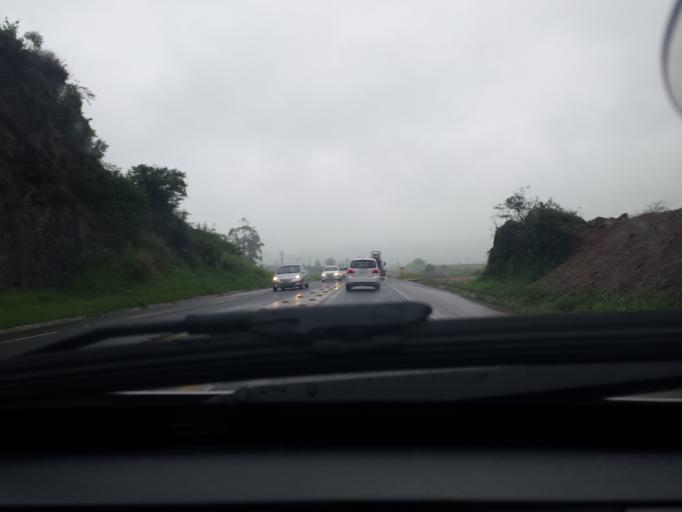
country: BR
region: Santa Catarina
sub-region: Itajai
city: Itajai
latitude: -26.8338
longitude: -48.7392
